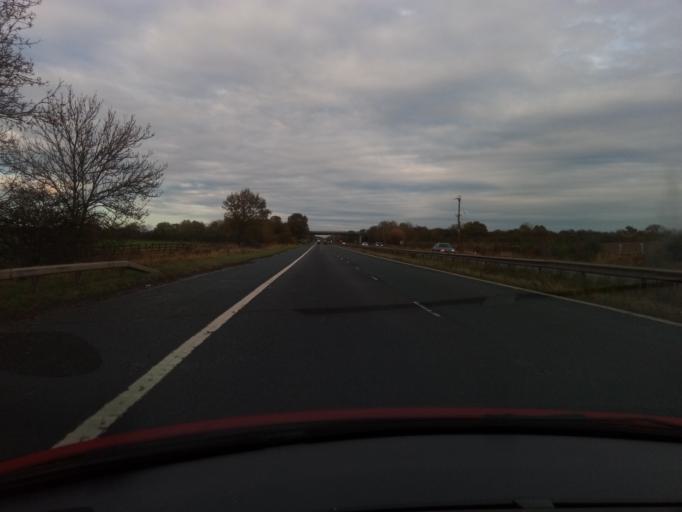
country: GB
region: England
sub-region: Darlington
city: High Coniscliffe
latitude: 54.5455
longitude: -1.6045
